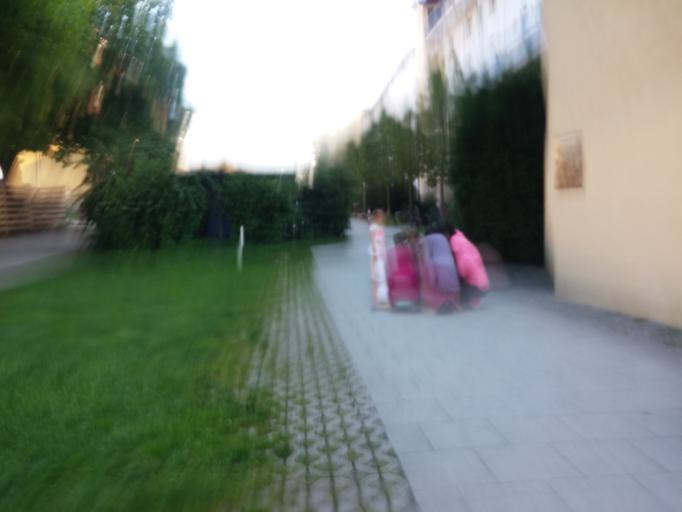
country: DE
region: Bavaria
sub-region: Upper Bavaria
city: Munich
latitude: 48.1119
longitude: 11.5370
